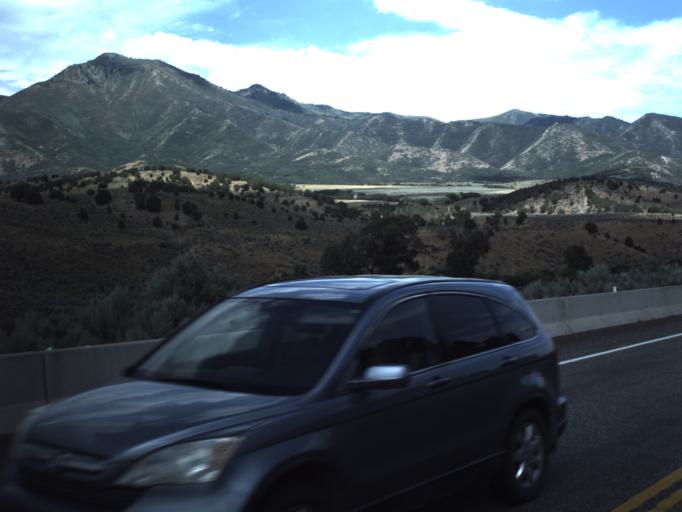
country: US
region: Utah
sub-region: Utah County
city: Woodland Hills
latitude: 39.9343
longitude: -111.5439
